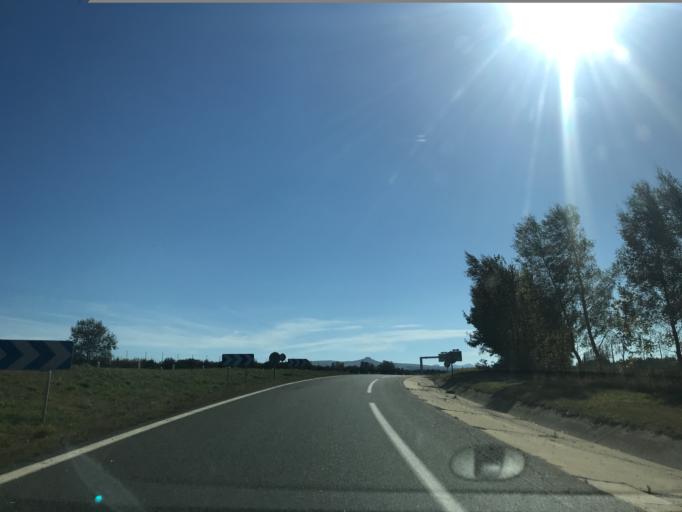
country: FR
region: Auvergne
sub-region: Departement du Puy-de-Dome
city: Saint-Sauves-d'Auvergne
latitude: 45.6707
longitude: 2.6787
